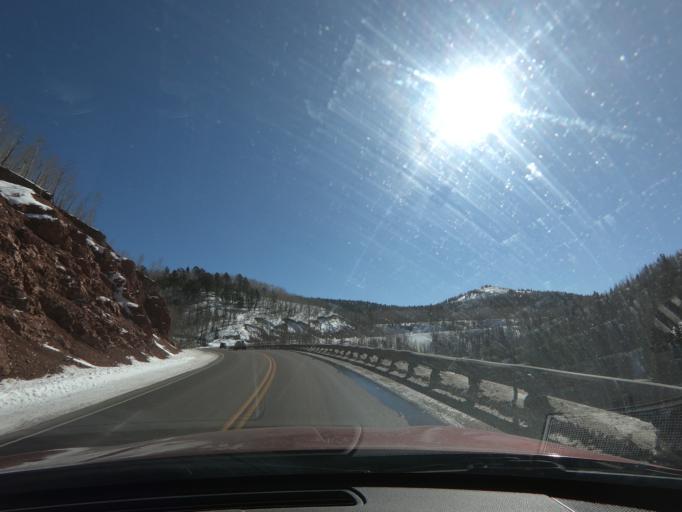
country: US
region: Colorado
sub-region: Teller County
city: Cripple Creek
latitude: 38.8026
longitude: -105.1208
